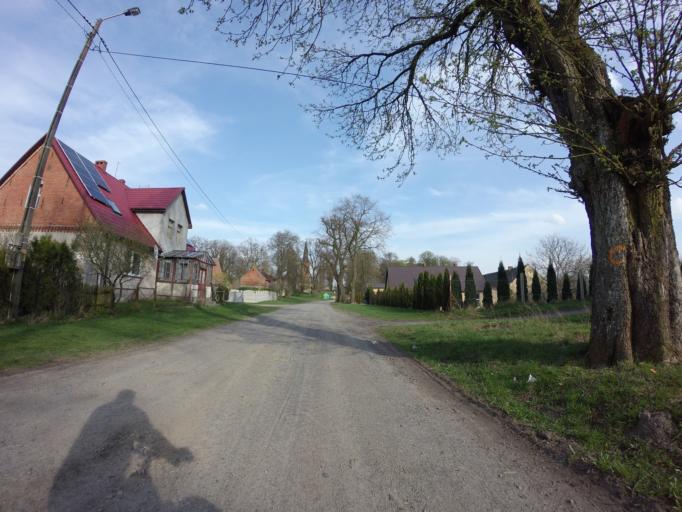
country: PL
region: West Pomeranian Voivodeship
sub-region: Powiat choszczenski
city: Recz
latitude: 53.1917
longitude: 15.5053
